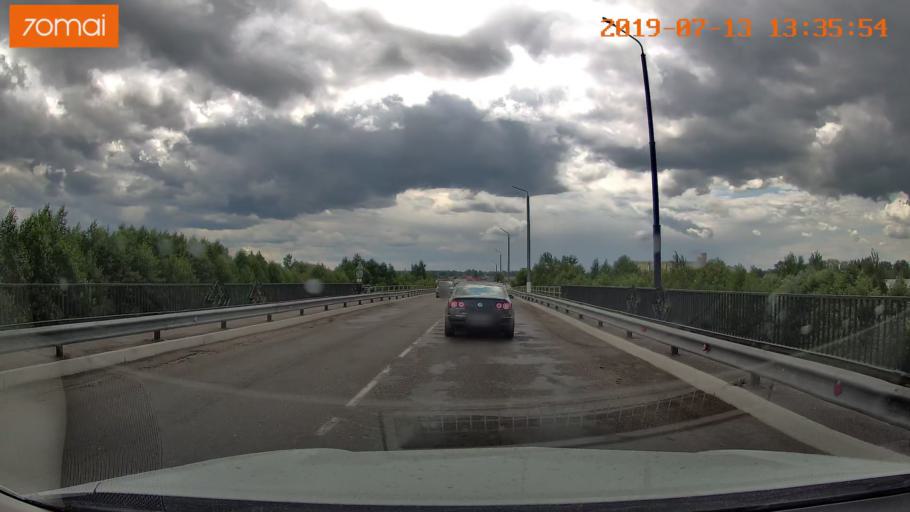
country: BY
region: Mogilev
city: Asipovichy
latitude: 53.3059
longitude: 28.6254
